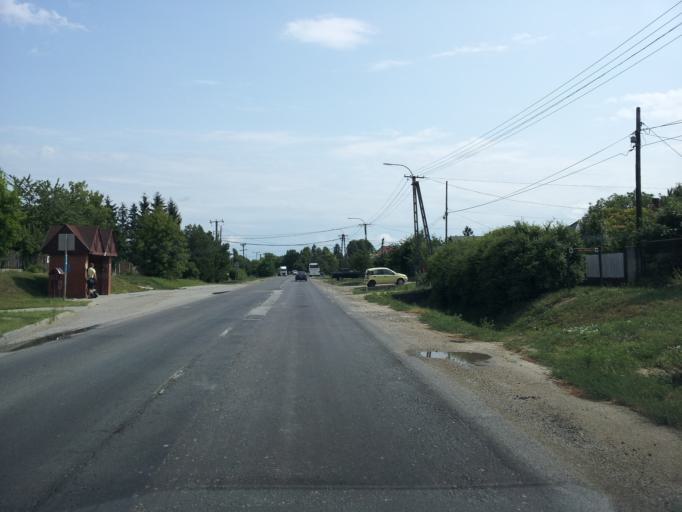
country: HU
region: Fejer
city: Enying
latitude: 46.9419
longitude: 18.2316
